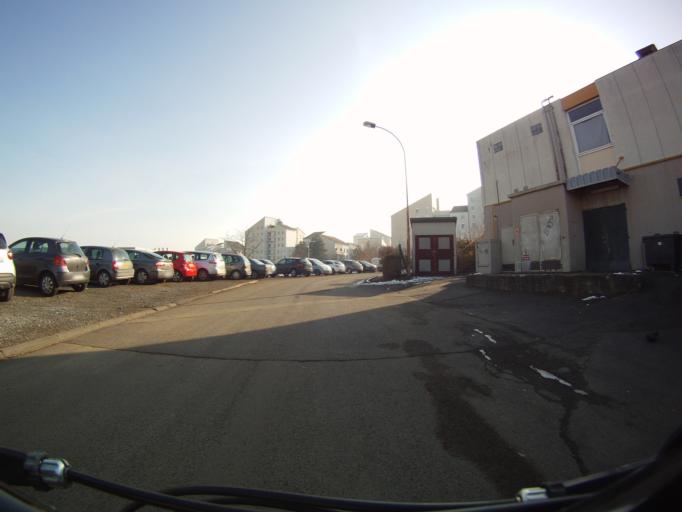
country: FR
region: Auvergne
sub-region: Departement du Puy-de-Dome
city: Beaumont
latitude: 45.7550
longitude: 3.0929
